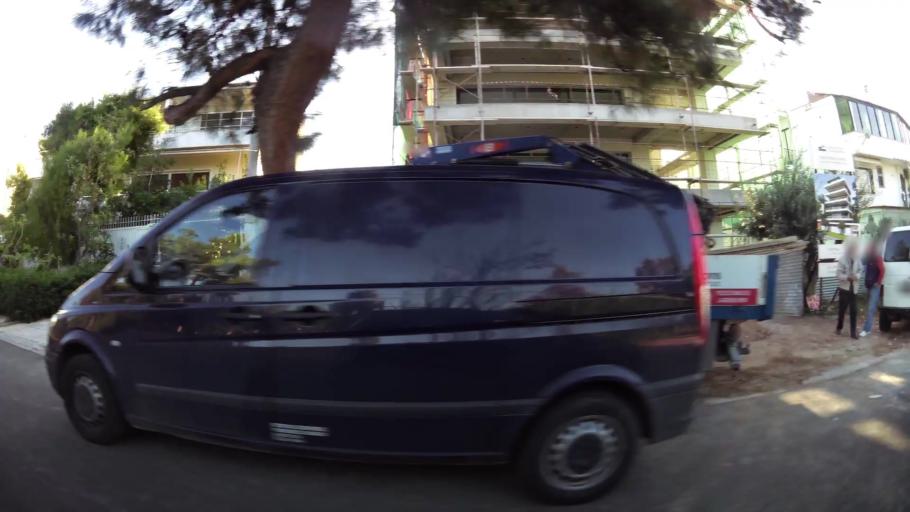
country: GR
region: Attica
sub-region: Nomarchia Athinas
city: Glyfada
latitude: 37.8768
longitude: 23.7494
